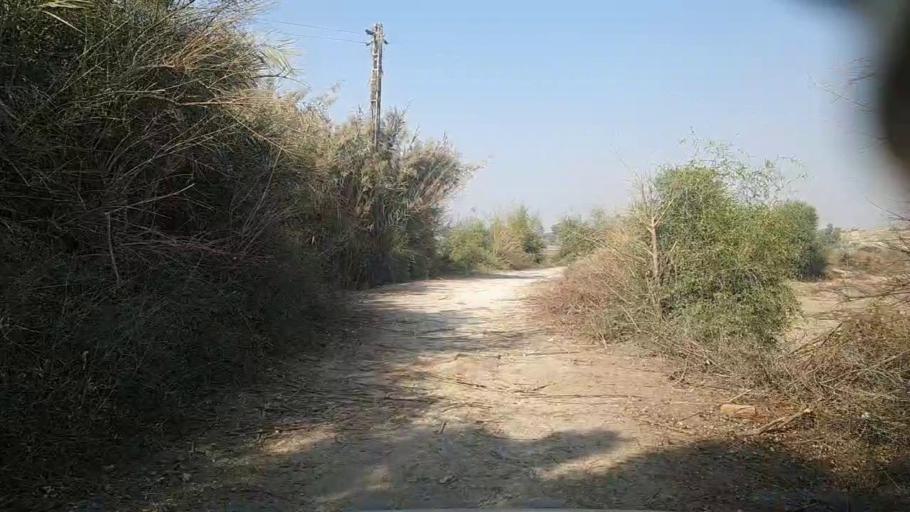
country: PK
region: Sindh
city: Kandiari
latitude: 26.9407
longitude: 68.5322
